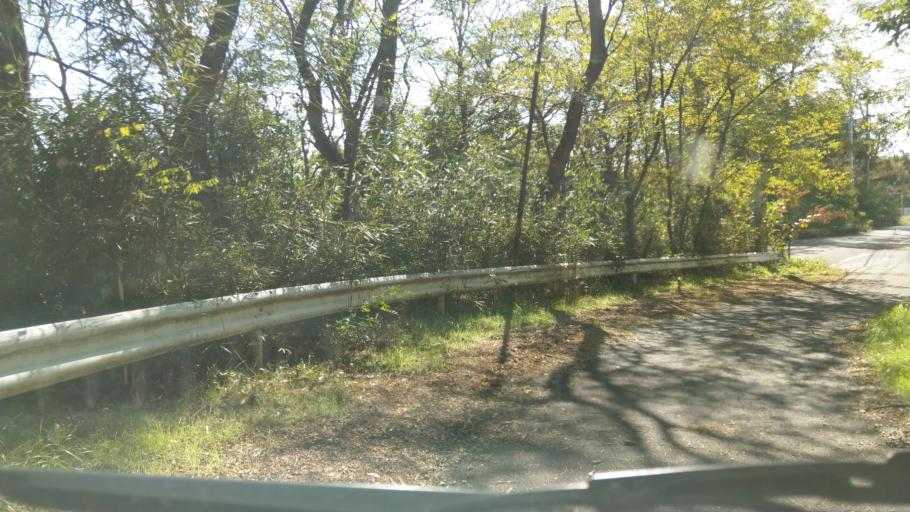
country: JP
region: Nagano
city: Komoro
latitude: 36.3542
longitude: 138.4026
